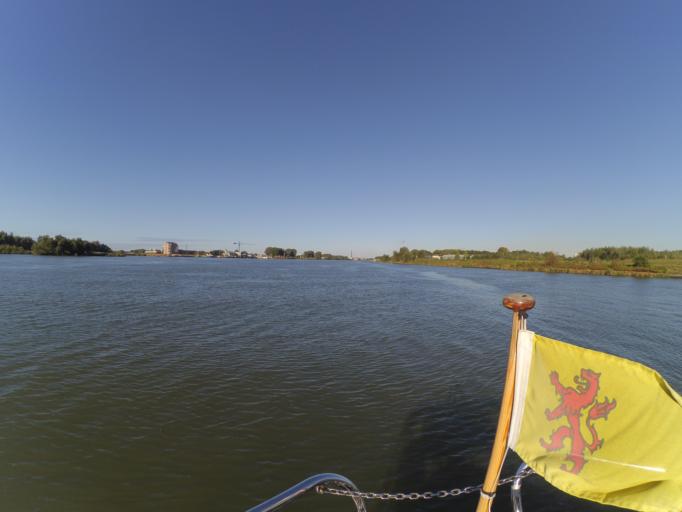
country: NL
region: South Holland
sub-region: Gemeente Zwijndrecht
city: Heerjansdam
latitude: 51.8077
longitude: 4.5876
